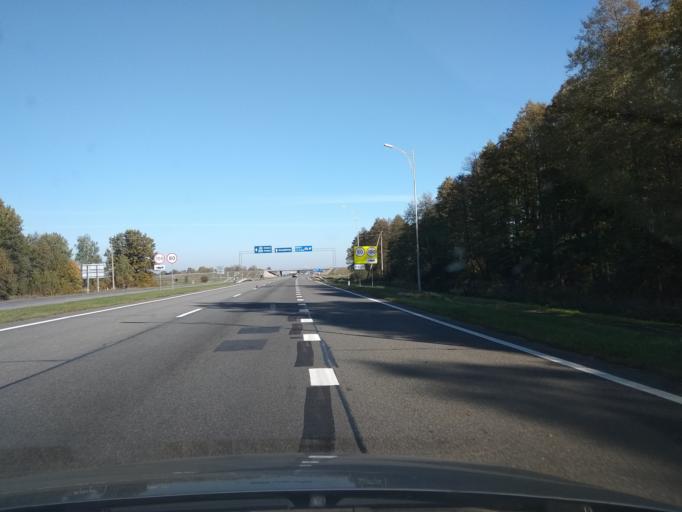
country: BY
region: Brest
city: Ivatsevichy
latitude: 52.6960
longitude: 25.3560
